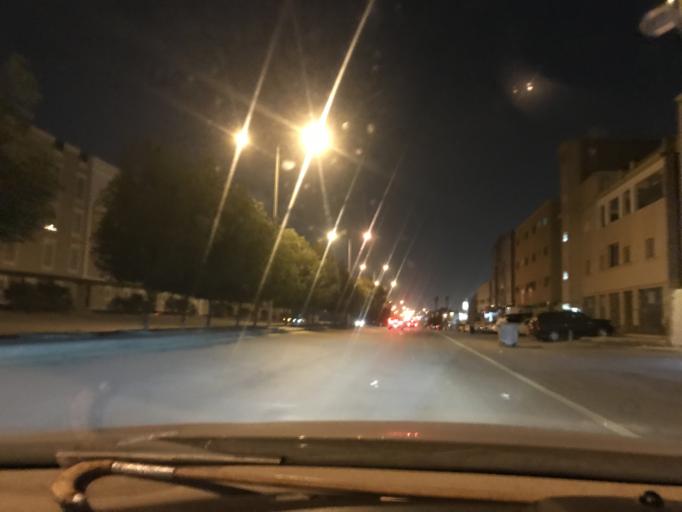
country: SA
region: Ar Riyad
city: Riyadh
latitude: 24.7553
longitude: 46.7549
